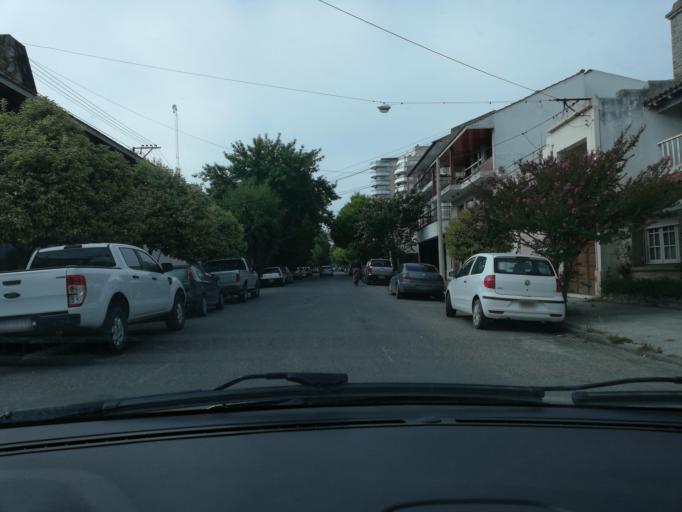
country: AR
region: Buenos Aires
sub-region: Partido de Balcarce
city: Balcarce
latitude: -37.8497
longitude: -58.2535
